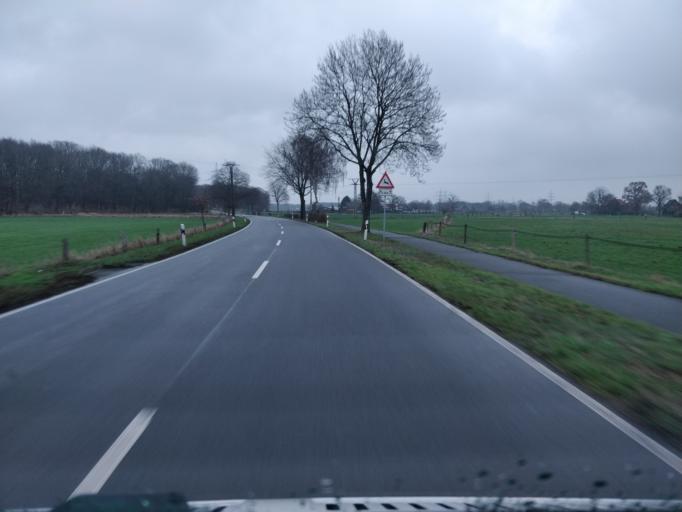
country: DE
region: North Rhine-Westphalia
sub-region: Regierungsbezirk Dusseldorf
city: Mehrhoog
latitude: 51.7581
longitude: 6.5026
